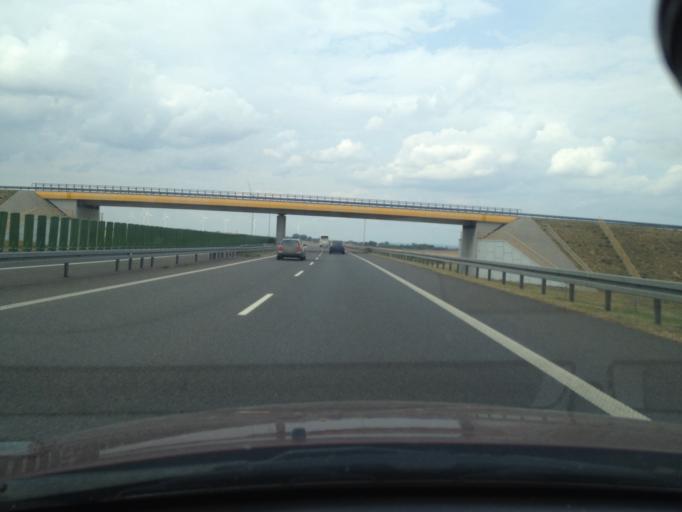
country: PL
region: West Pomeranian Voivodeship
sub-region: Powiat pyrzycki
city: Kozielice
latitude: 53.0791
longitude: 14.8552
